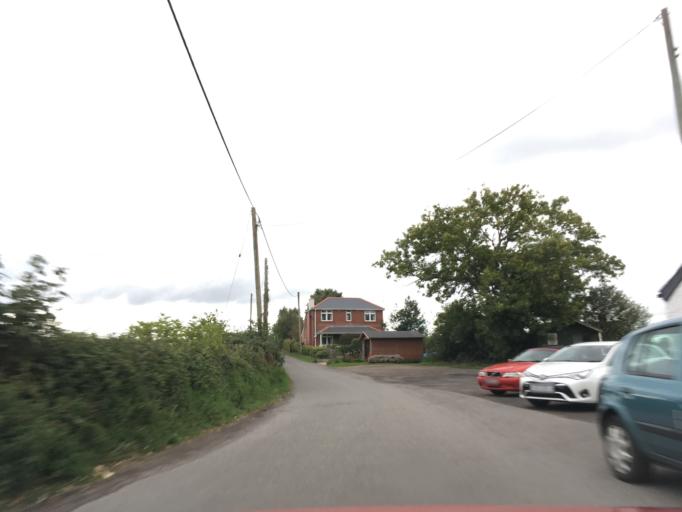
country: GB
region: Wales
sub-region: Newport
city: Caerleon
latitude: 51.6301
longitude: -2.9361
